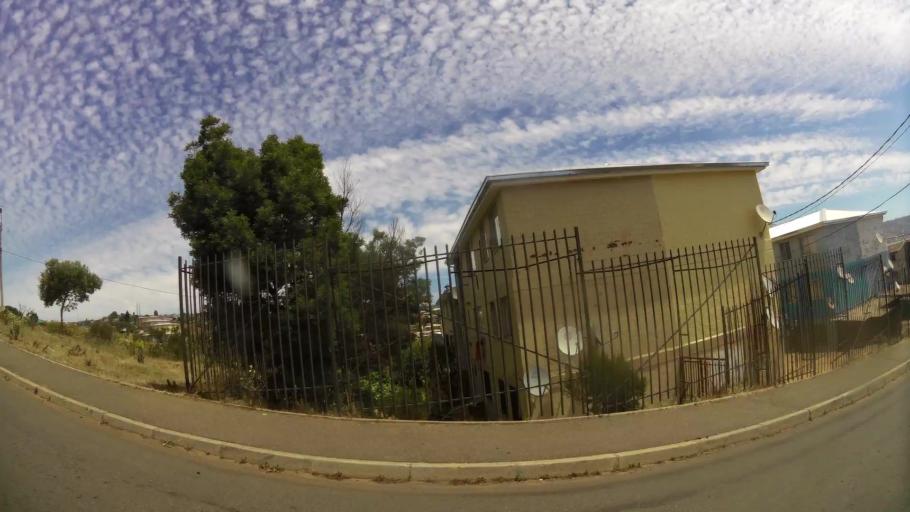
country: CL
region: Valparaiso
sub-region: Provincia de Valparaiso
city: Vina del Mar
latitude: -33.0544
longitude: -71.5728
